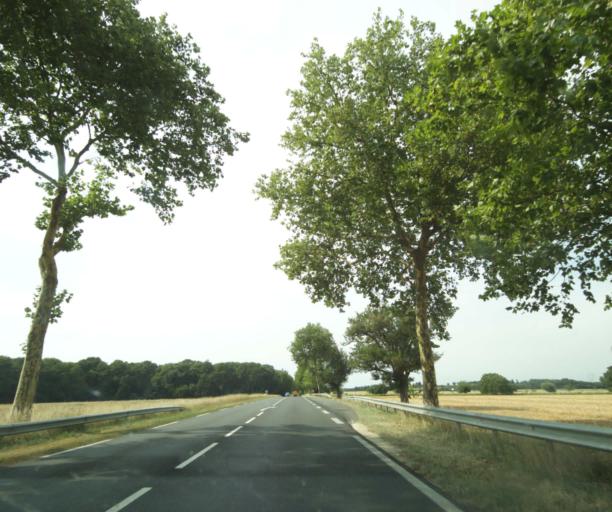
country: FR
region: Centre
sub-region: Departement d'Indre-et-Loire
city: Saint-Antoine-du-Rocher
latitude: 47.5046
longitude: 0.5980
